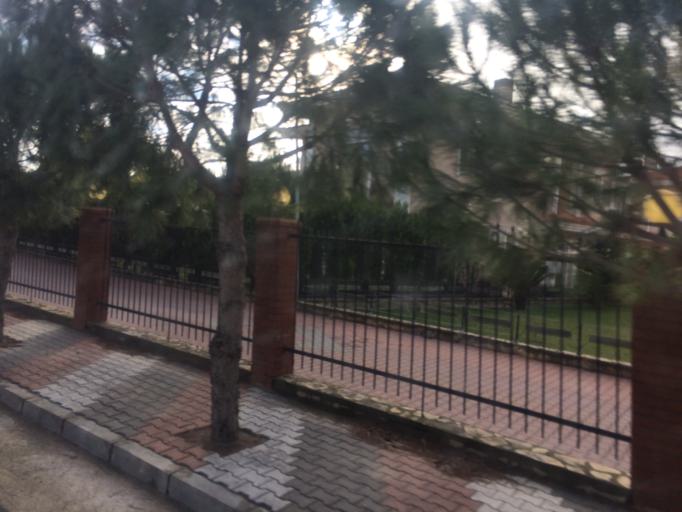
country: TR
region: Izmir
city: Menemen
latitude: 38.5039
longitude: 26.9591
